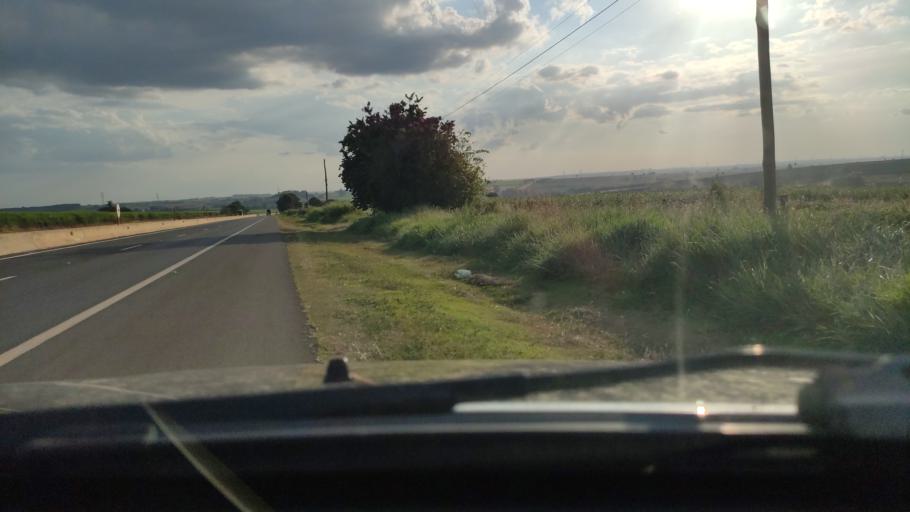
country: BR
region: Sao Paulo
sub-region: Artur Nogueira
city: Artur Nogueira
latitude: -22.4715
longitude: -47.1207
